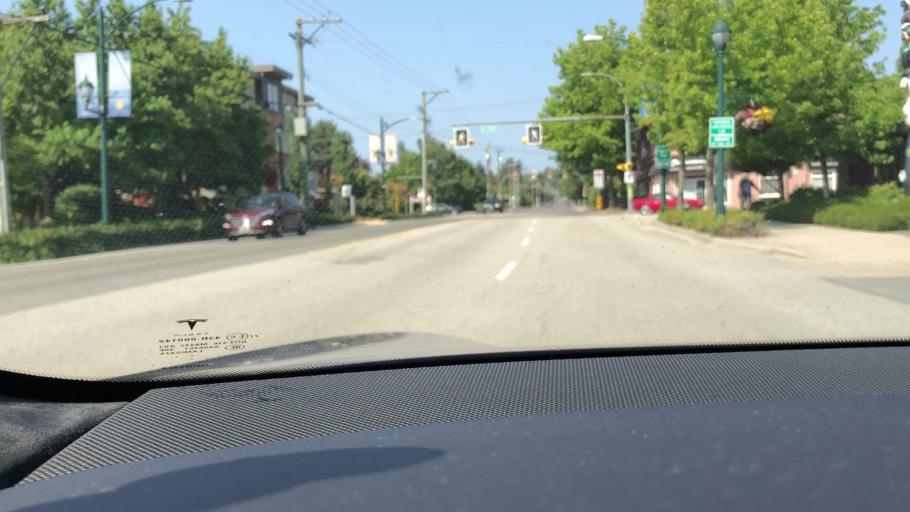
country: US
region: Washington
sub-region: Whatcom County
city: Point Roberts
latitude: 49.0248
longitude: -123.0715
